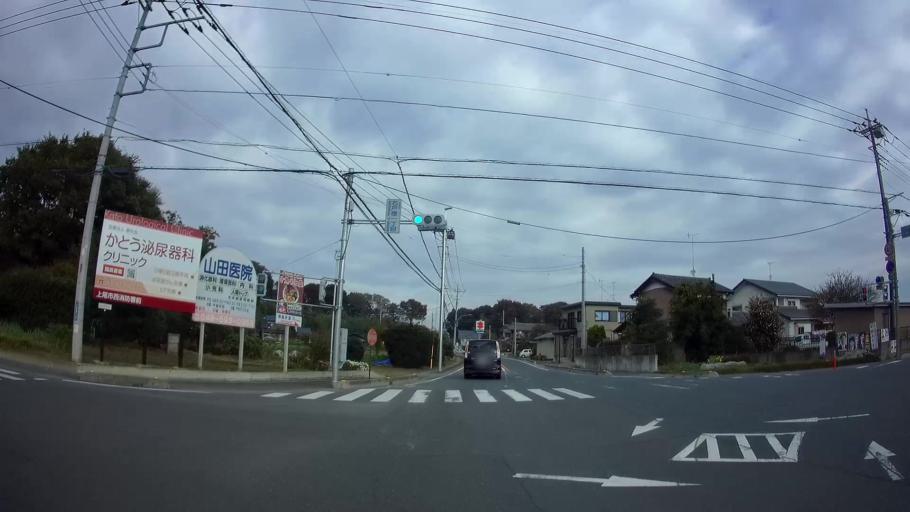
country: JP
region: Saitama
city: Okegawa
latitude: 36.0092
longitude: 139.5186
